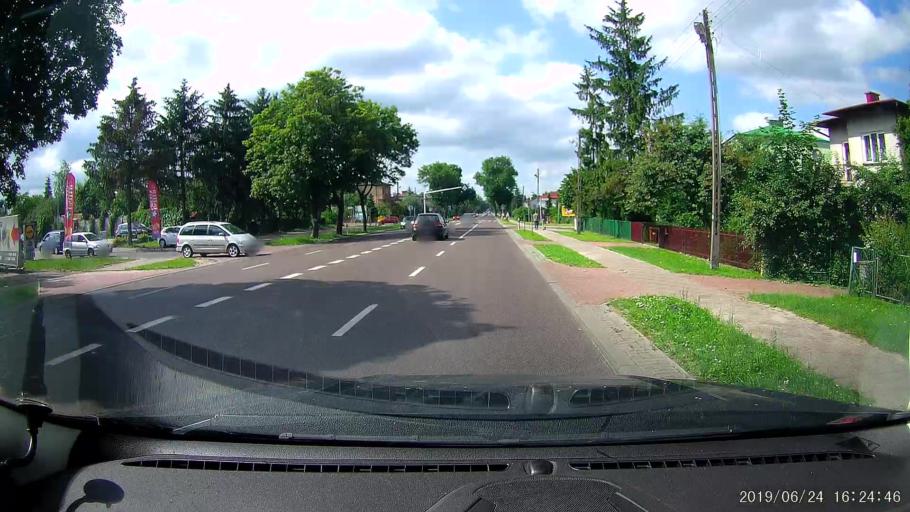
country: PL
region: Lublin Voivodeship
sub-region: Powiat tomaszowski
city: Tomaszow Lubelski
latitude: 50.4380
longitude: 23.4194
